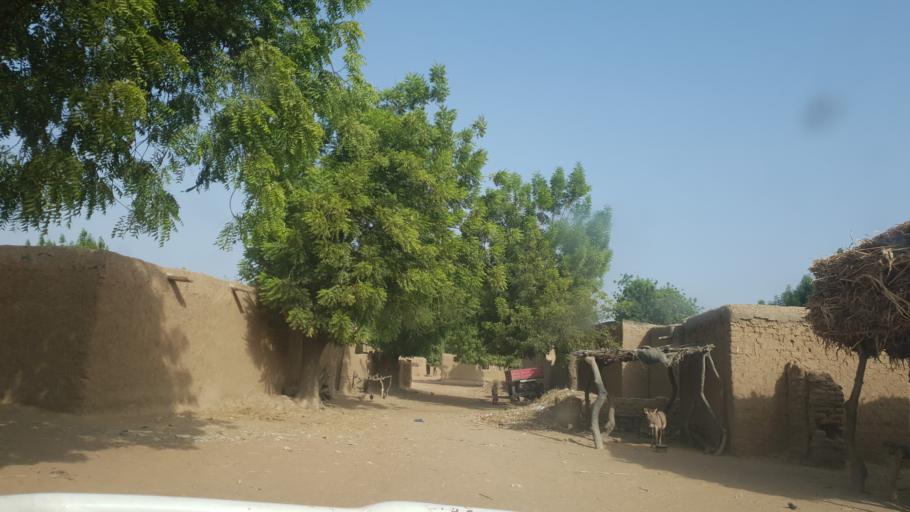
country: ML
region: Segou
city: Baroueli
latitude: 13.3534
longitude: -6.9316
